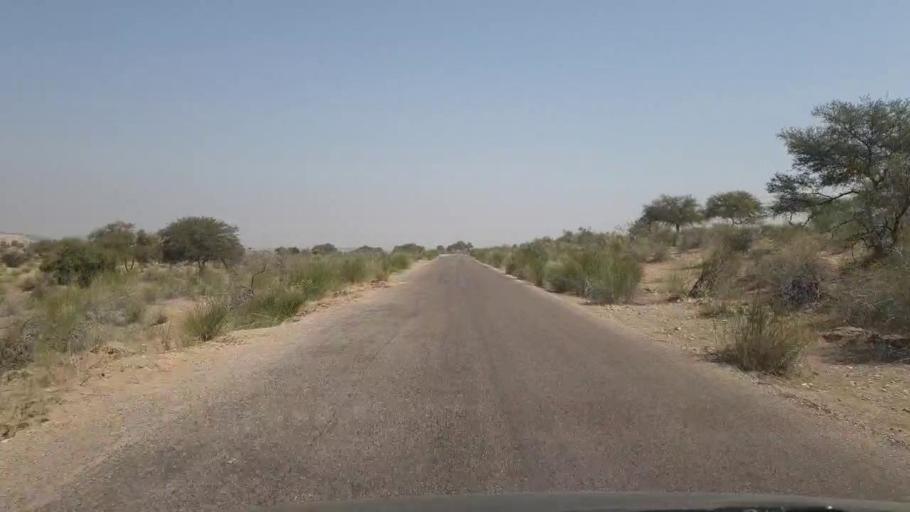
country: PK
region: Sindh
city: Chor
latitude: 25.6636
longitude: 70.1323
